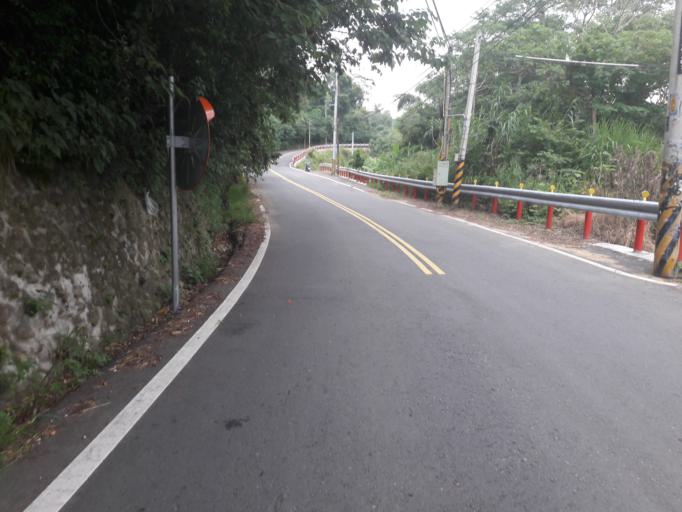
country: TW
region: Taiwan
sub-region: Hsinchu
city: Hsinchu
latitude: 24.7291
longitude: 120.9689
